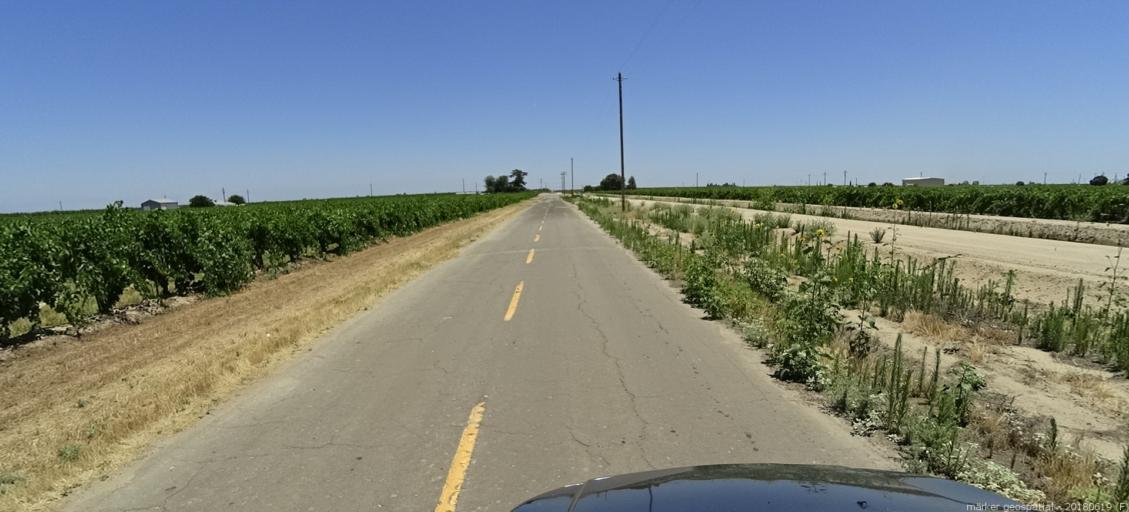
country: US
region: California
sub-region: Madera County
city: Parkwood
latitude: 36.8586
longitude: -120.0598
